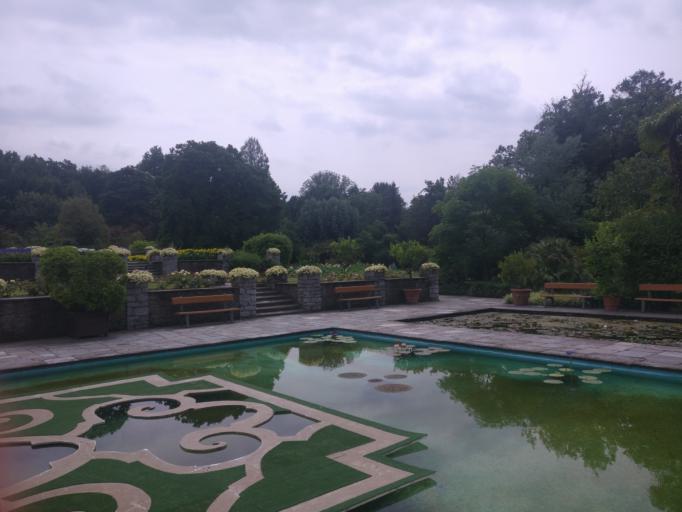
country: IT
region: Piedmont
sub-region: Provincia Verbano-Cusio-Ossola
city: Verbania
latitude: 45.9258
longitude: 8.5593
